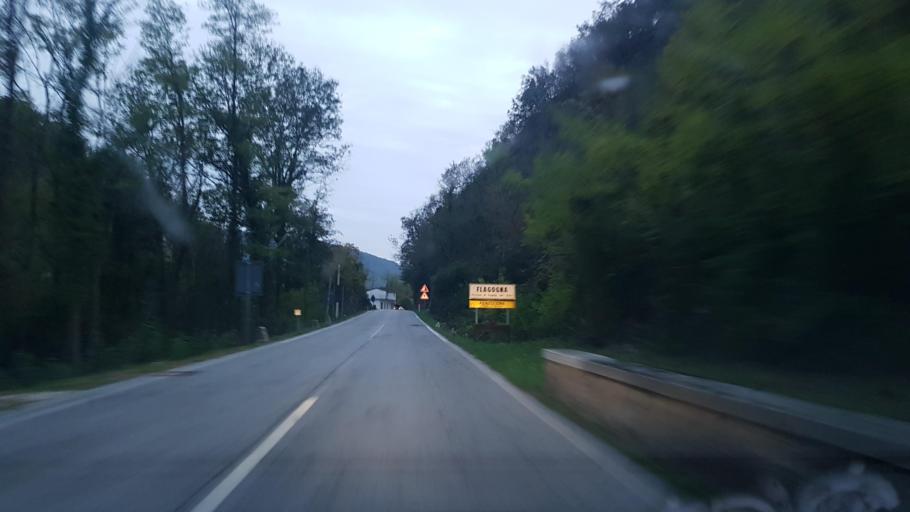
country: IT
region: Friuli Venezia Giulia
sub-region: Provincia di Pordenone
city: Anduins
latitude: 46.2134
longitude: 12.9551
